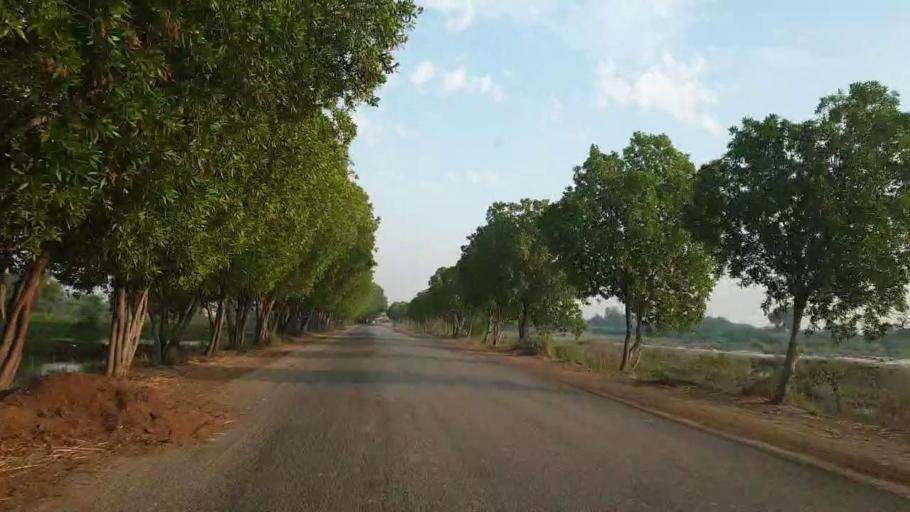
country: PK
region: Sindh
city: Tando Bago
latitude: 24.7170
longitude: 68.9397
